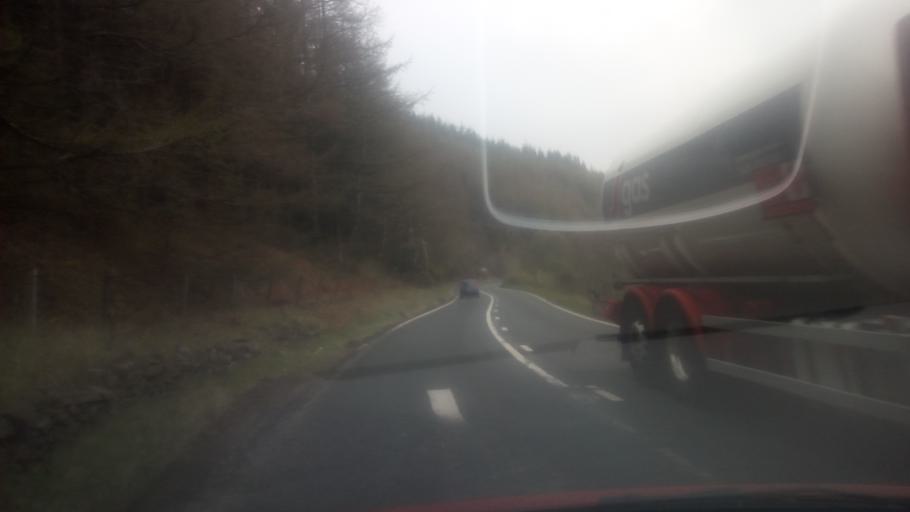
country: GB
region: Scotland
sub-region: The Scottish Borders
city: Galashiels
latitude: 55.7076
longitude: -2.8861
